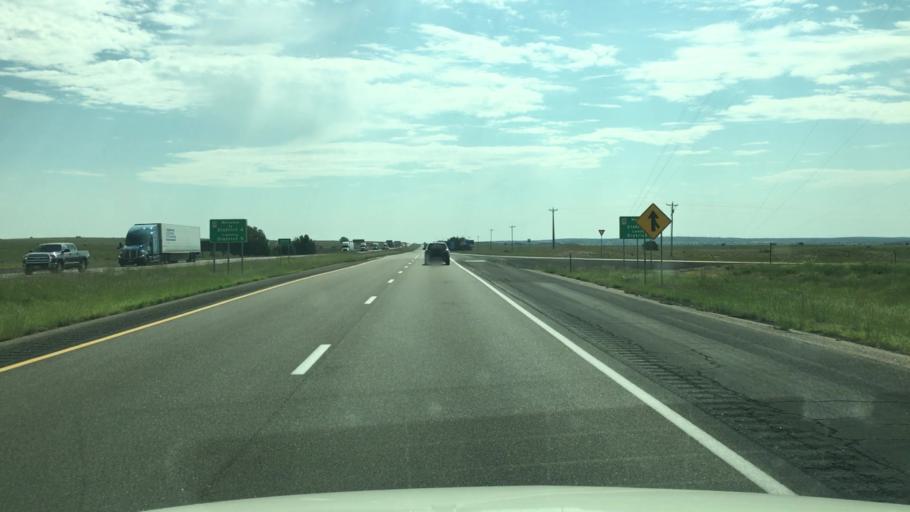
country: US
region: New Mexico
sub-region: San Miguel County
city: Las Vegas
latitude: 34.9912
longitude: -105.2918
